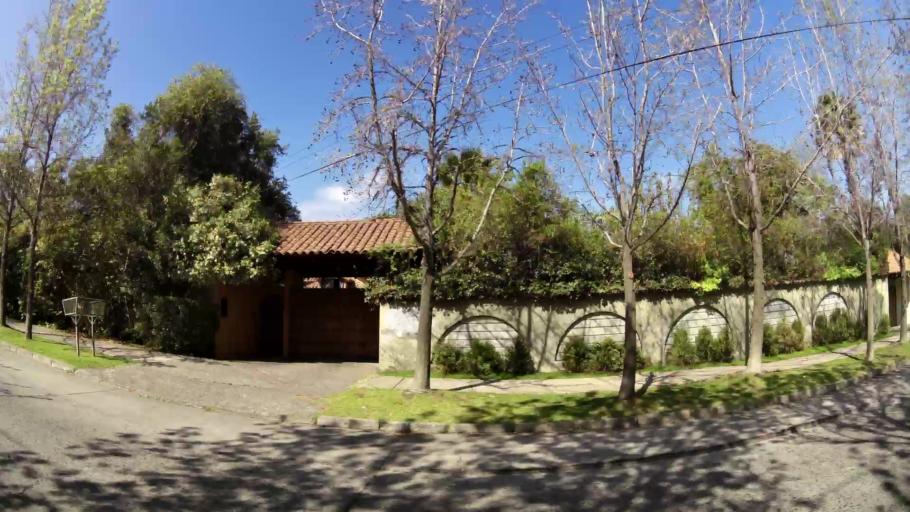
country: CL
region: Santiago Metropolitan
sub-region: Provincia de Santiago
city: Villa Presidente Frei, Nunoa, Santiago, Chile
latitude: -33.4445
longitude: -70.5400
